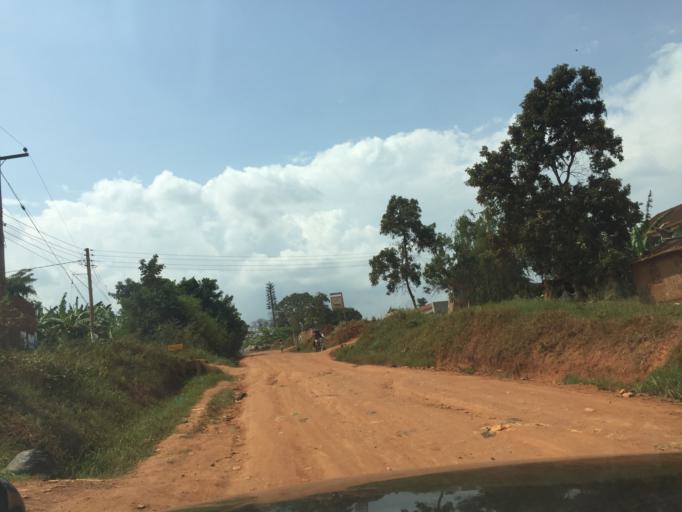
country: UG
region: Central Region
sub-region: Wakiso District
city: Kireka
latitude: 0.3969
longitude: 32.6229
